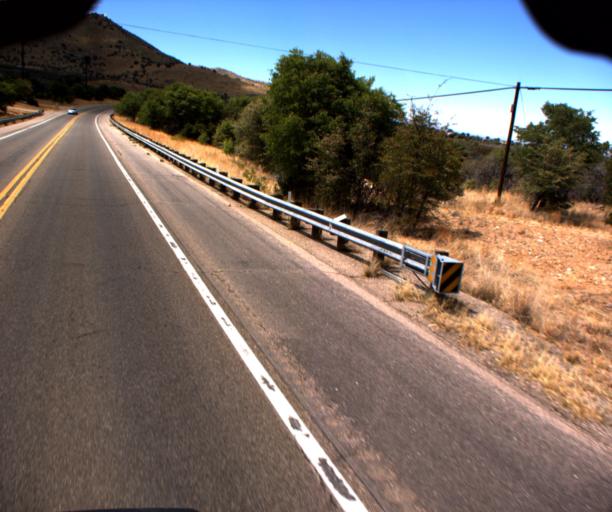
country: US
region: Arizona
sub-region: Cochise County
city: Sierra Vista Southeast
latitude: 31.3961
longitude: -110.2371
